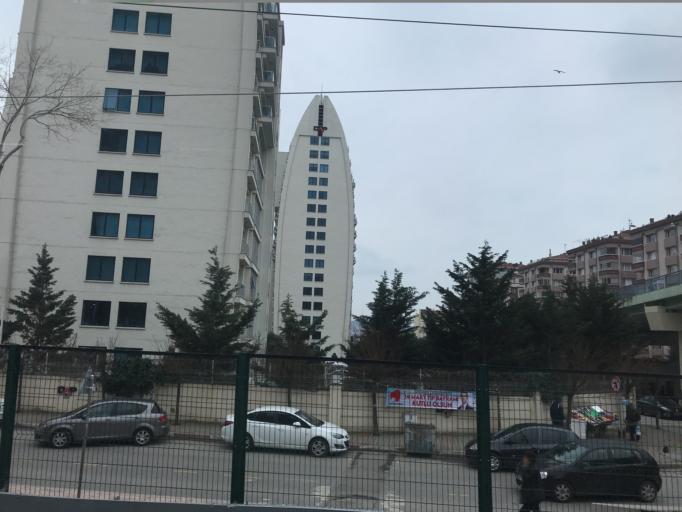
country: TR
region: Istanbul
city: Maltepe
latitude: 40.8984
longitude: 29.1694
